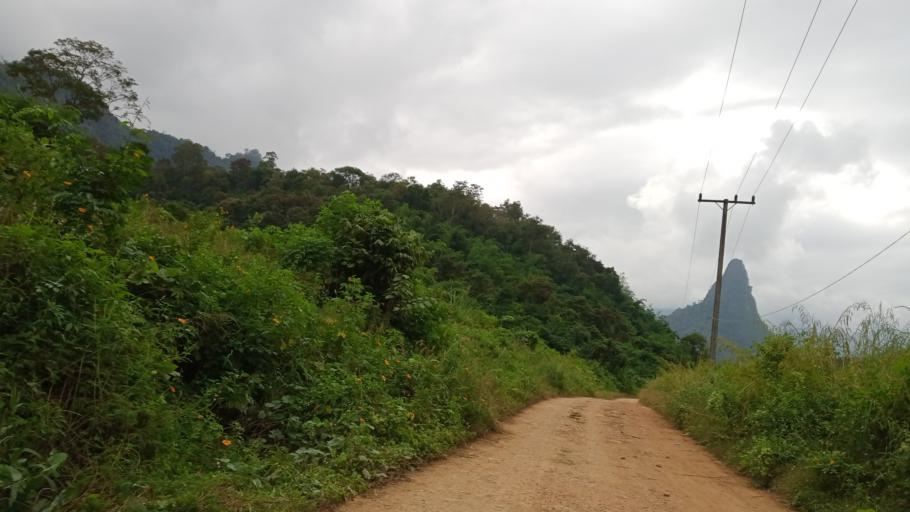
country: LA
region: Xiangkhoang
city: Phonsavan
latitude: 19.0862
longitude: 103.0091
